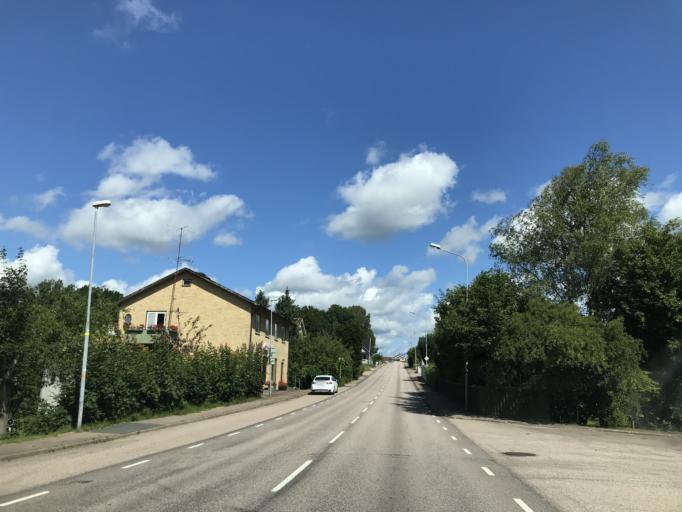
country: SE
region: Halland
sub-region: Laholms Kommun
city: Knared
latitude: 56.5176
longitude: 13.3165
